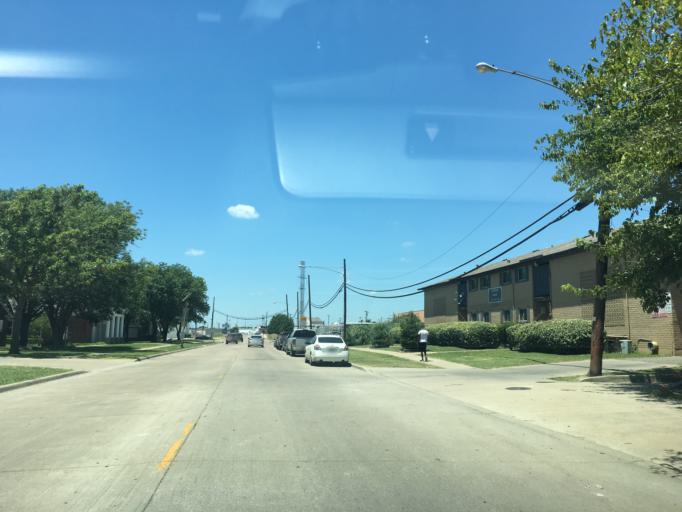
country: US
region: Texas
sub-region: Dallas County
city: Garland
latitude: 32.8507
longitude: -96.6771
